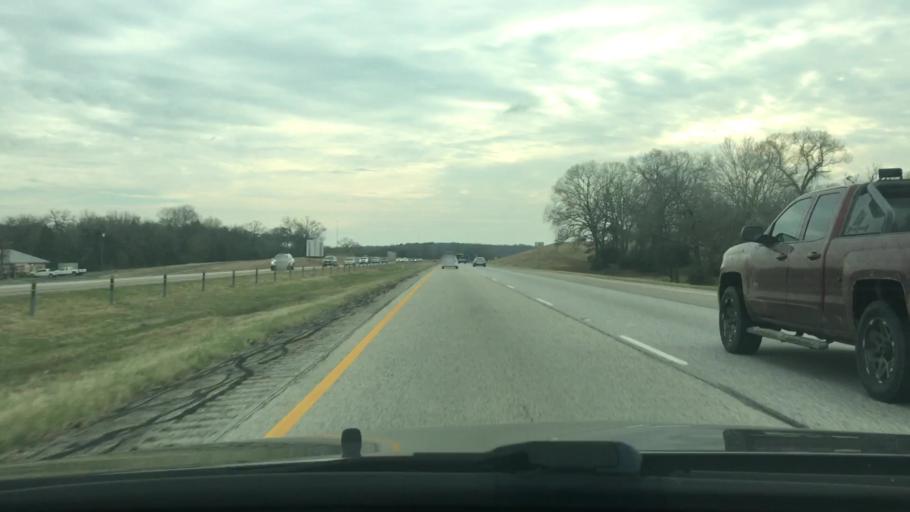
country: US
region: Texas
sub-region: Leon County
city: Centerville
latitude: 31.2533
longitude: -95.9885
